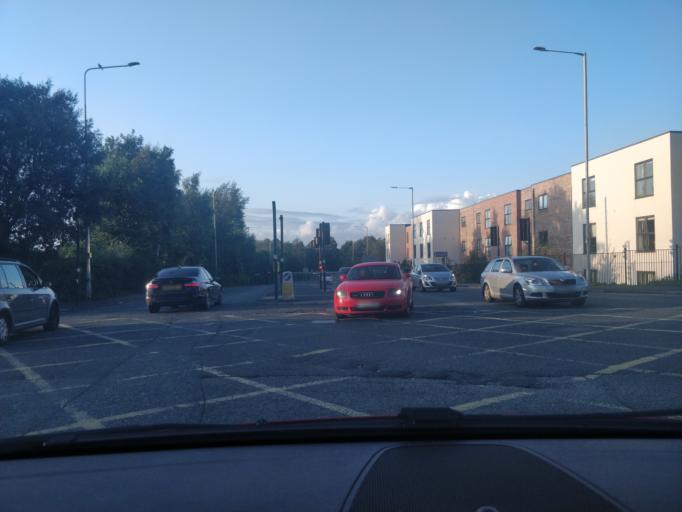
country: GB
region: England
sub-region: Lancashire
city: Preston
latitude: 53.7745
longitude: -2.6899
